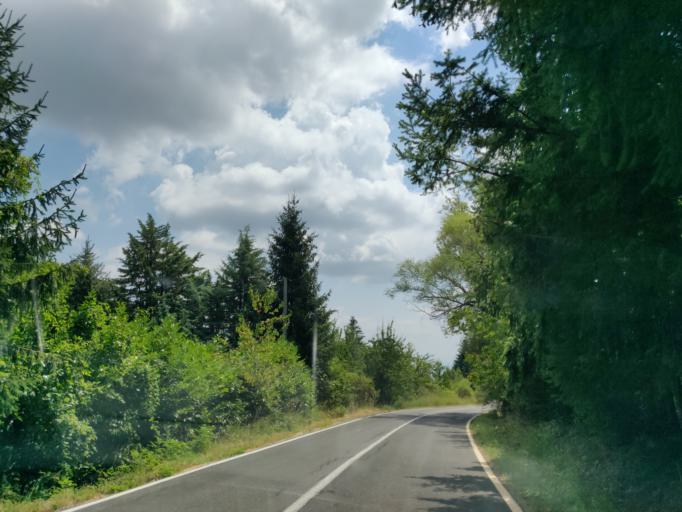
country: IT
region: Tuscany
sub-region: Provincia di Siena
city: Abbadia San Salvatore
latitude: 42.8945
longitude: 11.6551
